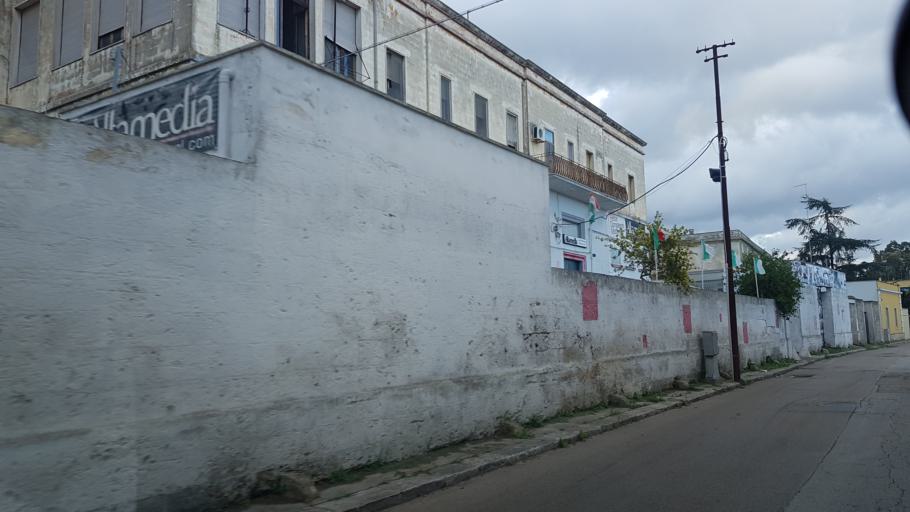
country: IT
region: Apulia
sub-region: Provincia di Brindisi
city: San Pietro Vernotico
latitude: 40.4886
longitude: 18.0016
